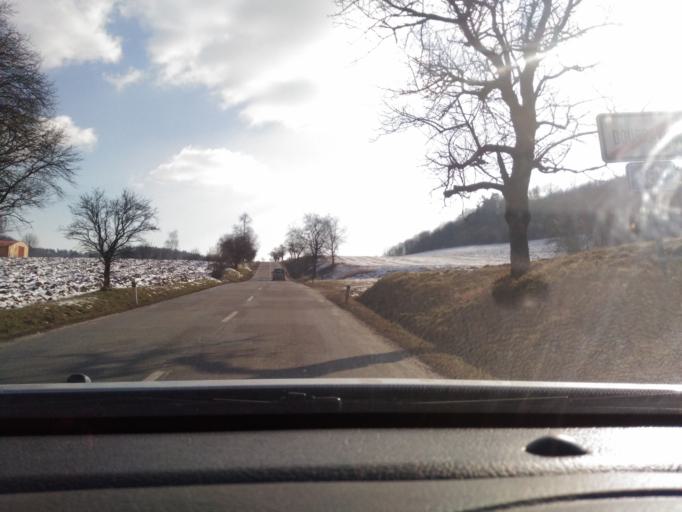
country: CZ
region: South Moravian
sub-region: Okres Brno-Venkov
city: Nedvedice
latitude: 49.4159
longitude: 16.3517
